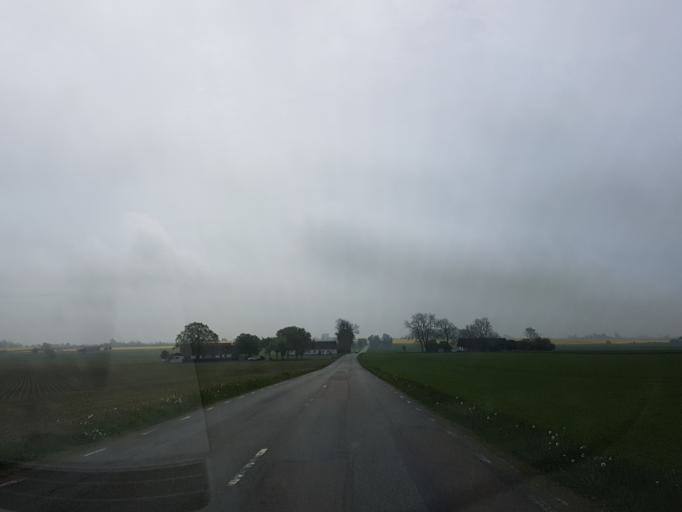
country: SE
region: Skane
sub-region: Tomelilla Kommun
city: Tomelilla
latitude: 55.4827
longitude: 14.1011
